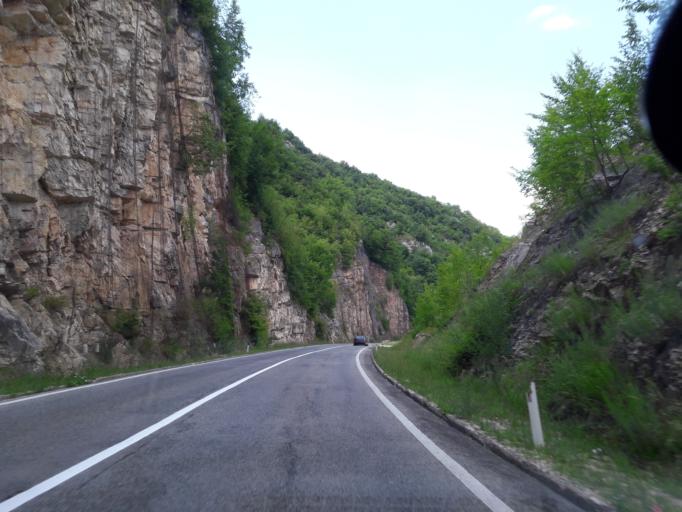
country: BA
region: Republika Srpska
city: Mrkonjic Grad
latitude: 44.4937
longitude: 17.1523
